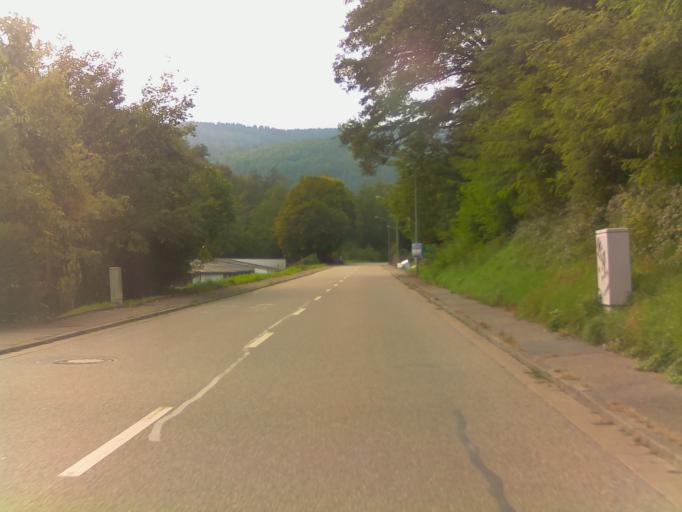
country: DE
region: Hesse
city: Hirschhorn
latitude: 49.4490
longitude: 8.8916
